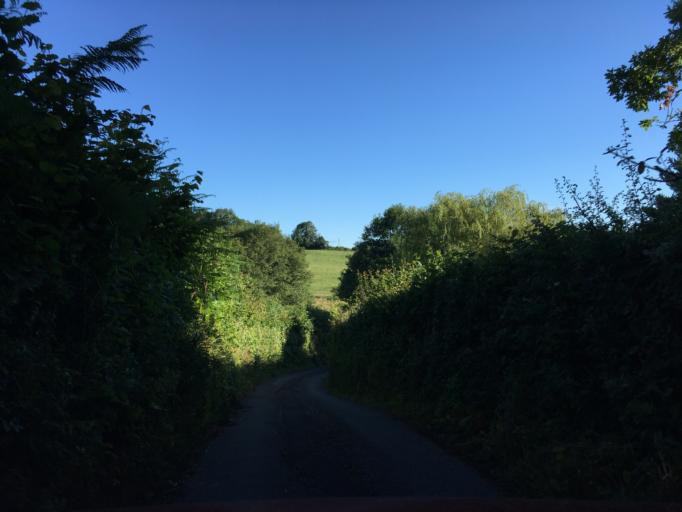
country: GB
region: Wales
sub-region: Monmouthshire
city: Tintern
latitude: 51.6852
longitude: -2.7358
